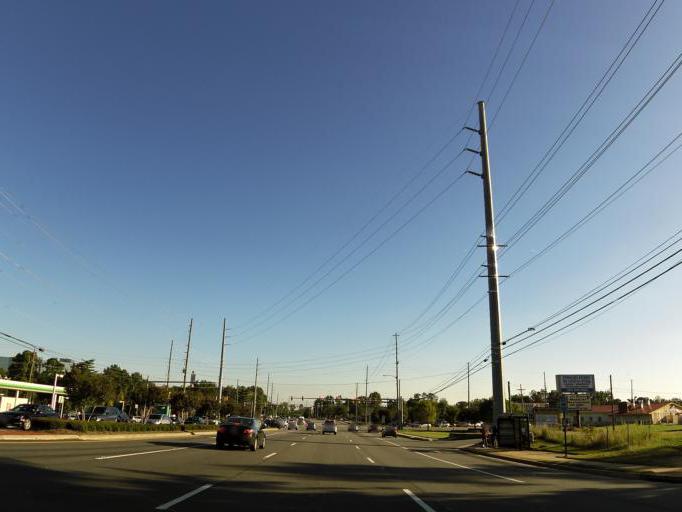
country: US
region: Georgia
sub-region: Cobb County
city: Vinings
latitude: 33.9192
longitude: -84.4672
